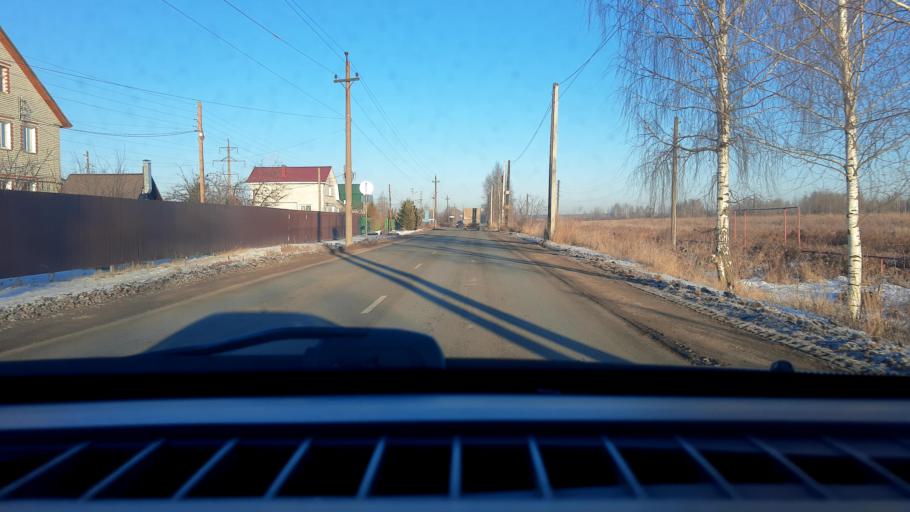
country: RU
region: Nizjnij Novgorod
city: Bor
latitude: 56.3799
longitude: 44.0806
